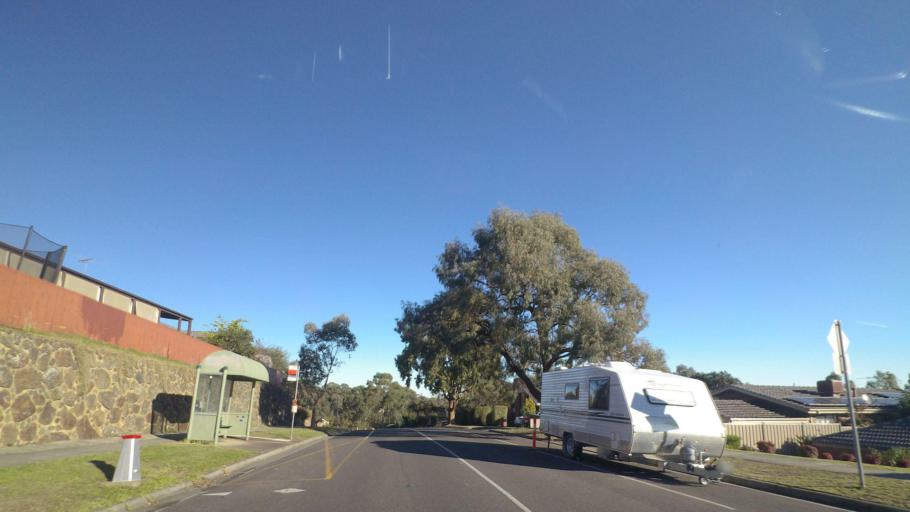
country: AU
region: Victoria
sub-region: Banyule
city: Greensborough
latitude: -37.6879
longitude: 145.1053
